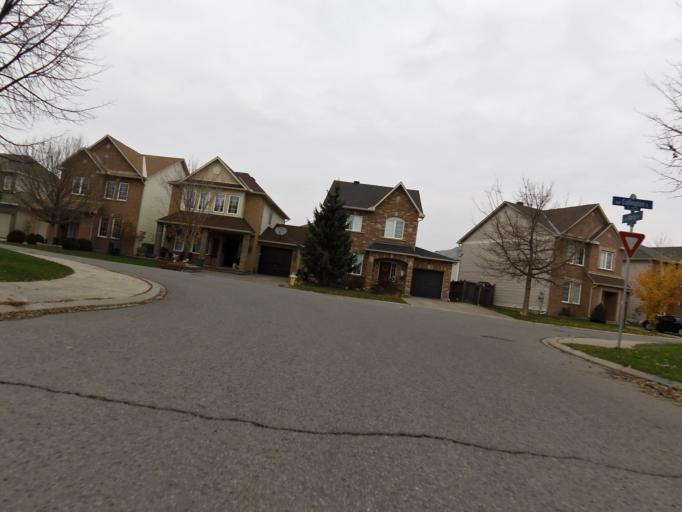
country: CA
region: Ontario
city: Bells Corners
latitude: 45.2728
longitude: -75.7062
